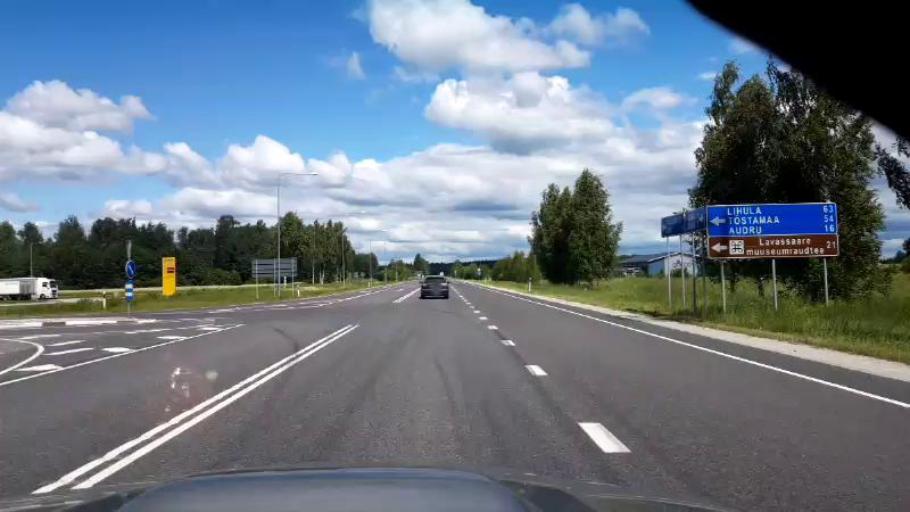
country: EE
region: Paernumaa
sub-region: Sauga vald
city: Sauga
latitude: 58.4497
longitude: 24.5031
